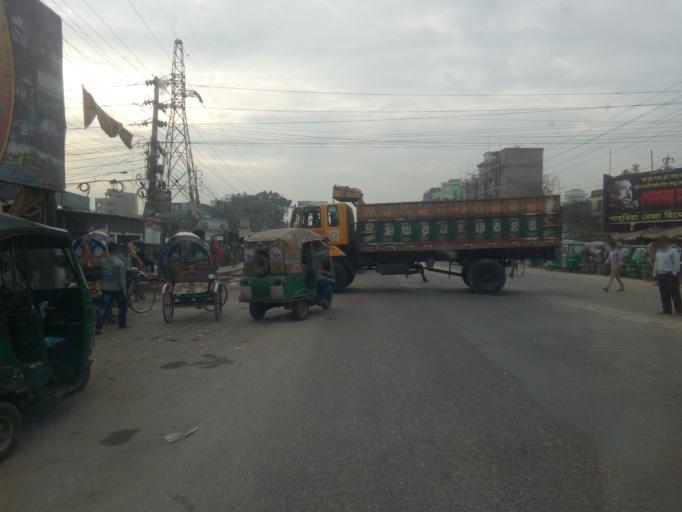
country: BD
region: Dhaka
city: Narayanganj
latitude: 23.6442
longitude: 90.4937
